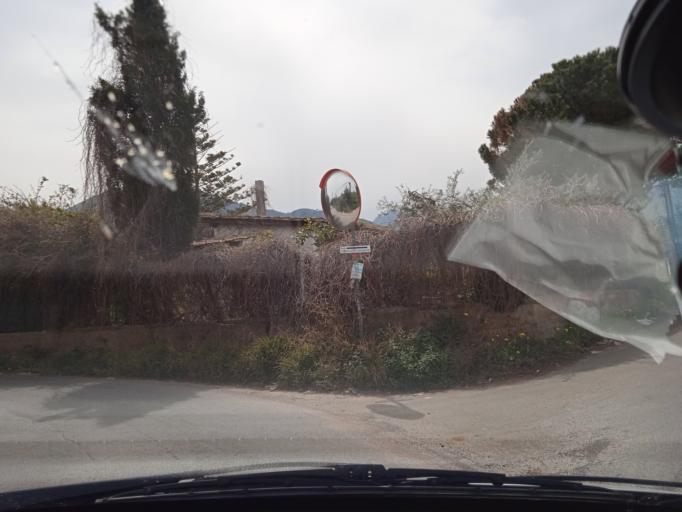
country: IT
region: Sicily
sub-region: Palermo
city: Torre Colonna-Sperone
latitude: 38.0348
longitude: 13.5627
